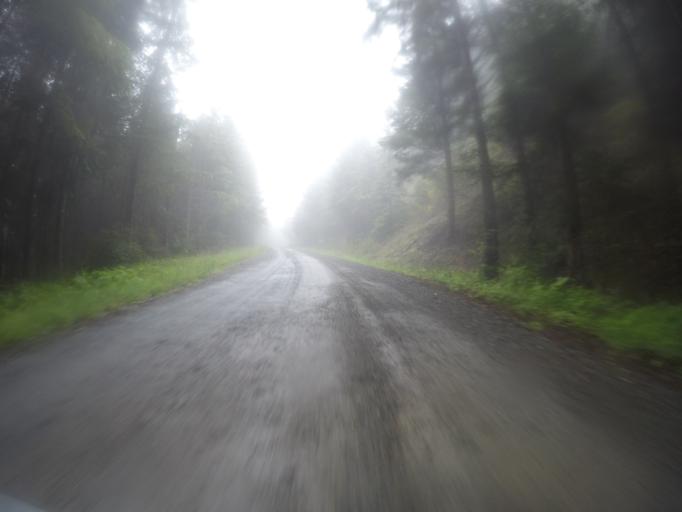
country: US
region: California
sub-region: Humboldt County
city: Westhaven-Moonstone
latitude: 41.2405
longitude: -123.9872
